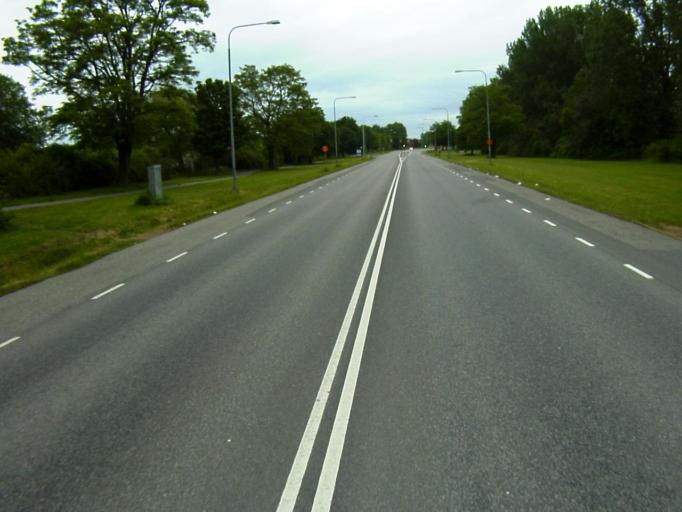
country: SE
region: Skane
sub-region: Kristianstads Kommun
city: Kristianstad
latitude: 56.0520
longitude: 14.1605
